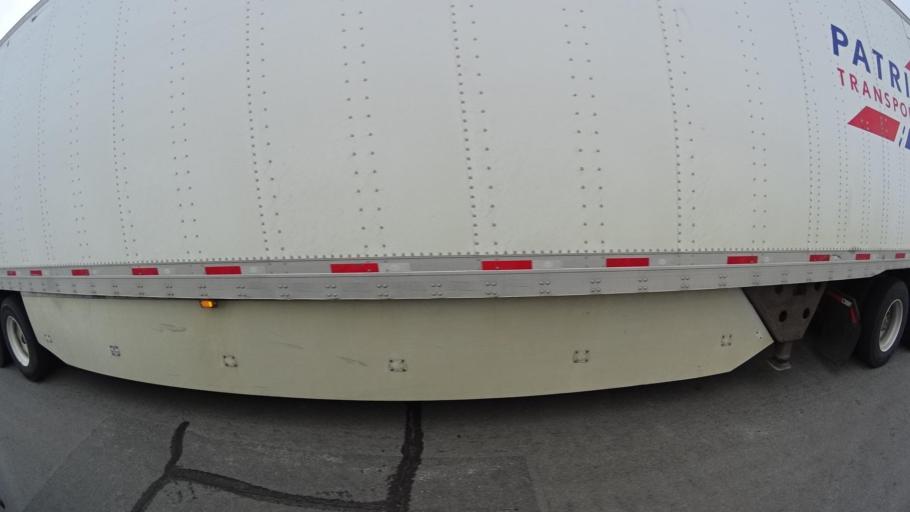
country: US
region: Nevada
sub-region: Washoe County
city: Spanish Springs
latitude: 39.6801
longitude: -119.7041
